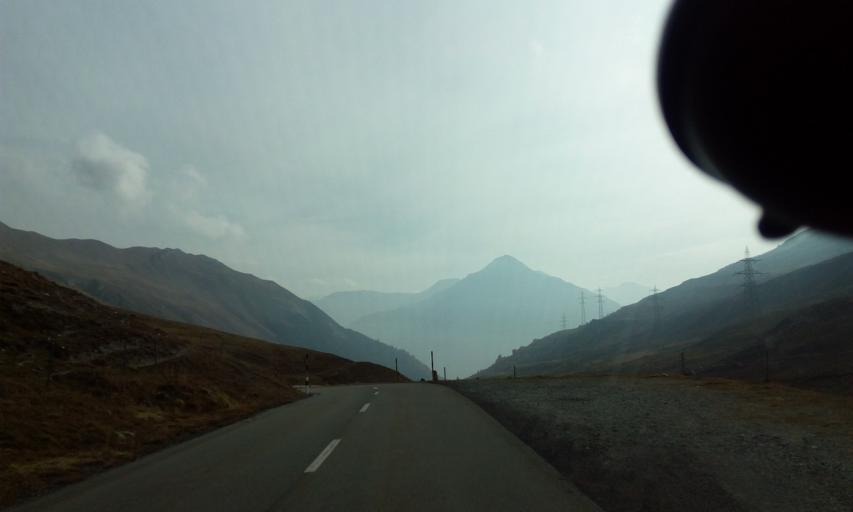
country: CH
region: Grisons
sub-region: Maloja District
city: Ponte
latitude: 46.5888
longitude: 9.8741
